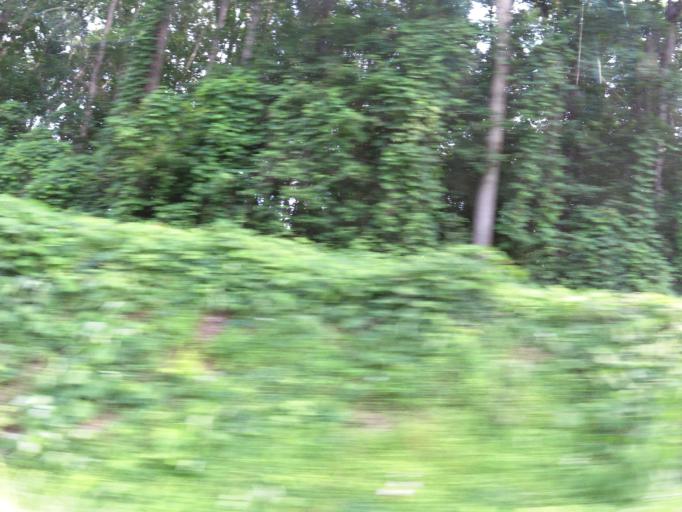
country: US
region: Tennessee
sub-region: Humphreys County
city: McEwen
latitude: 36.1033
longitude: -87.6771
